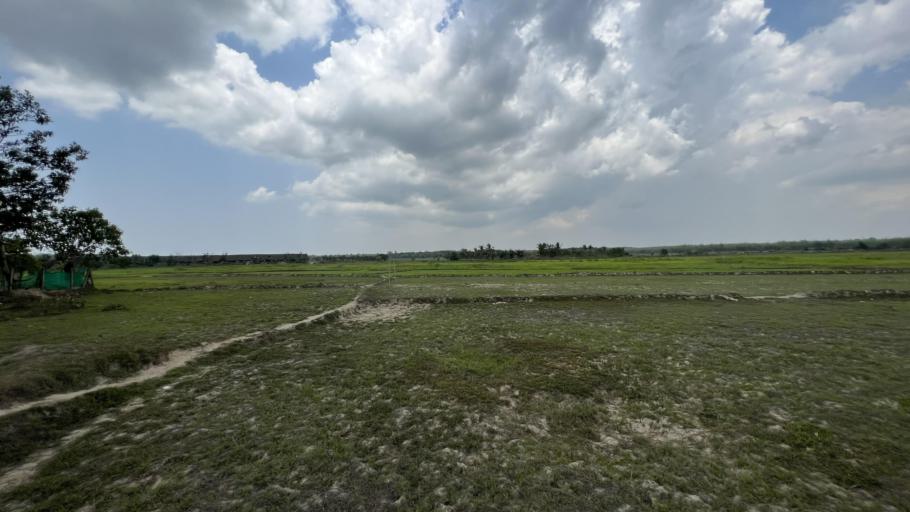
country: MM
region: Yangon
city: Twante
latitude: 16.5763
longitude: 95.9268
